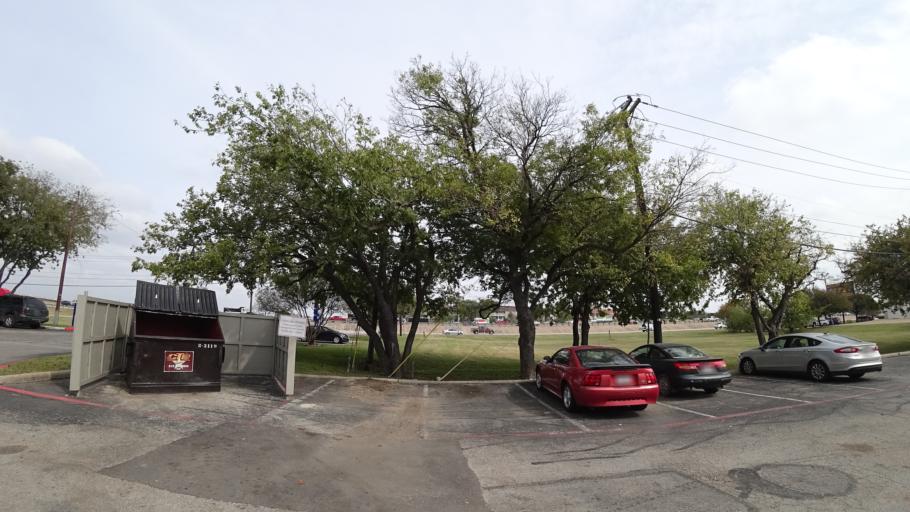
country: US
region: Texas
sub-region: Williamson County
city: Round Rock
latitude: 30.4965
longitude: -97.6808
